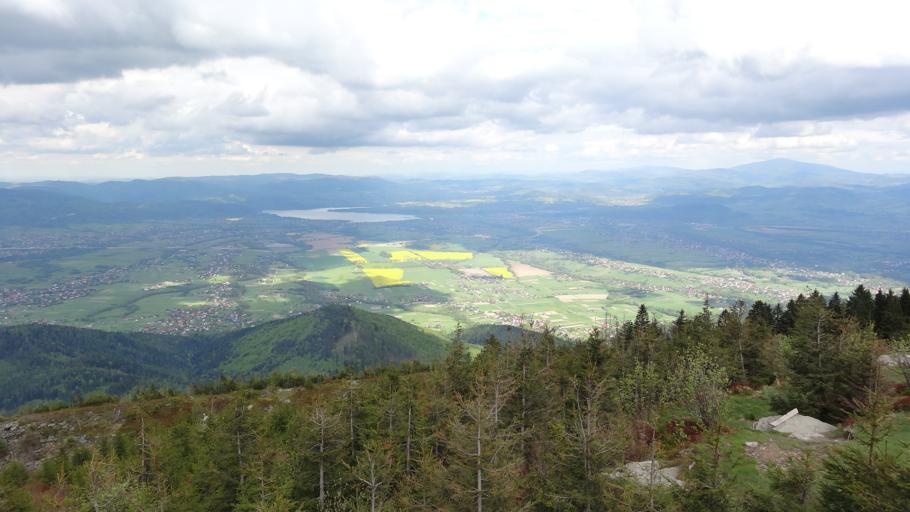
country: PL
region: Silesian Voivodeship
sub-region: Powiat bielski
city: Szczyrk
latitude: 49.6856
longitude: 19.0313
